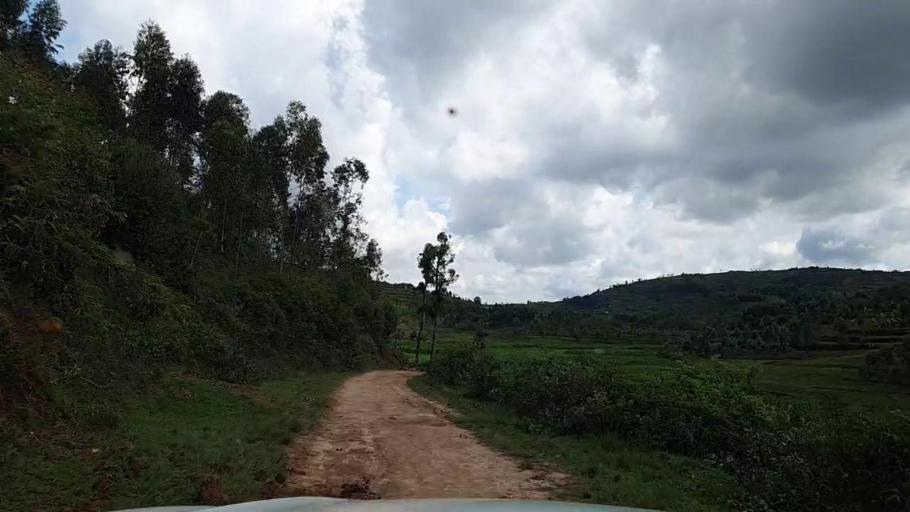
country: RW
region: Southern Province
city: Gikongoro
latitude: -2.3893
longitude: 29.5482
